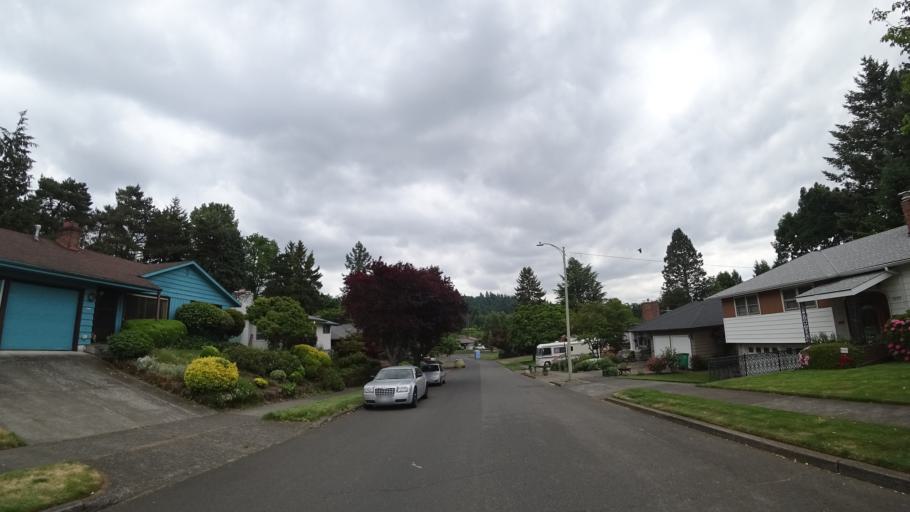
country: US
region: Oregon
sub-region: Multnomah County
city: Lents
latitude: 45.5084
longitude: -122.5571
